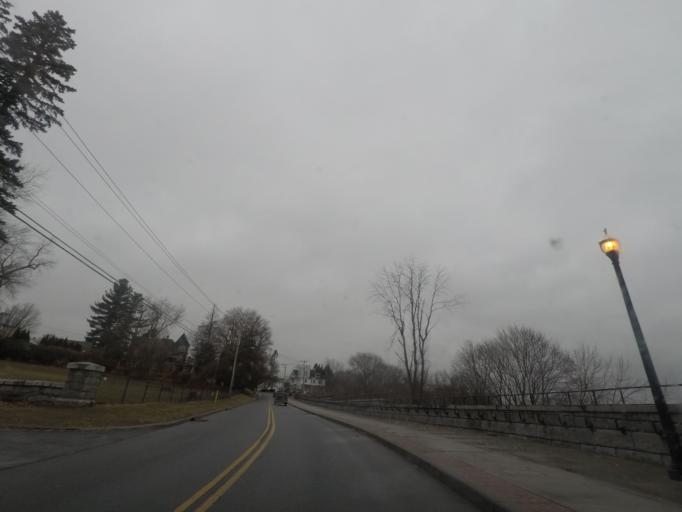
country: US
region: New York
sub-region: Saratoga County
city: Mechanicville
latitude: 42.9004
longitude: -73.6942
